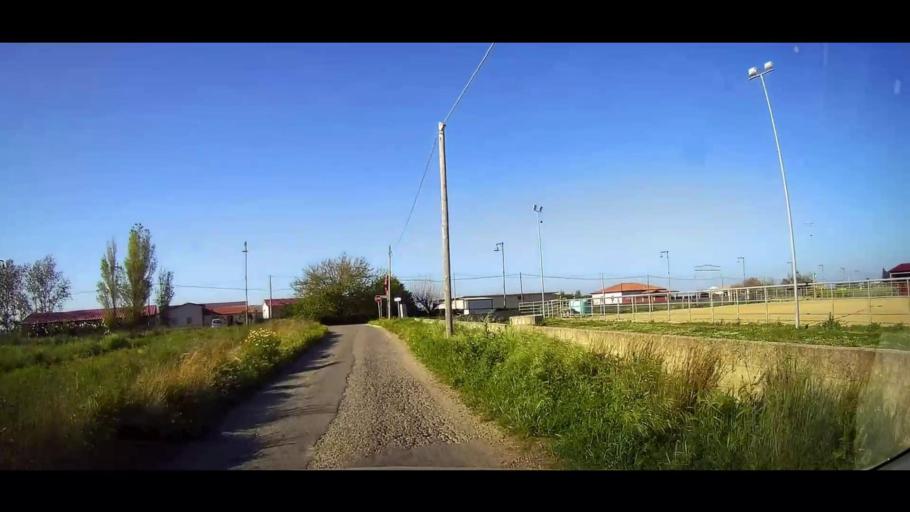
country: IT
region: Calabria
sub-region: Provincia di Crotone
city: Crotone
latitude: 39.0248
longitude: 17.1877
